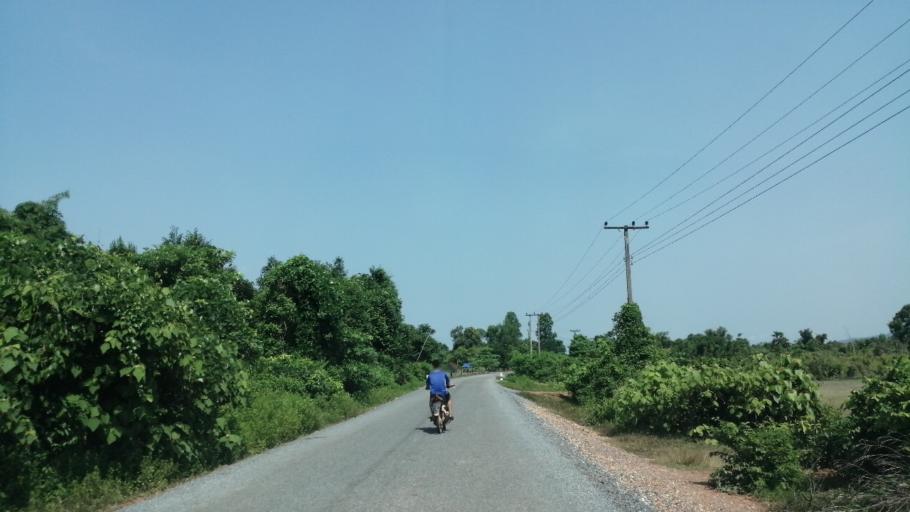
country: LA
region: Bolikhamxai
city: Bolikhan
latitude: 18.4506
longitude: 103.8082
